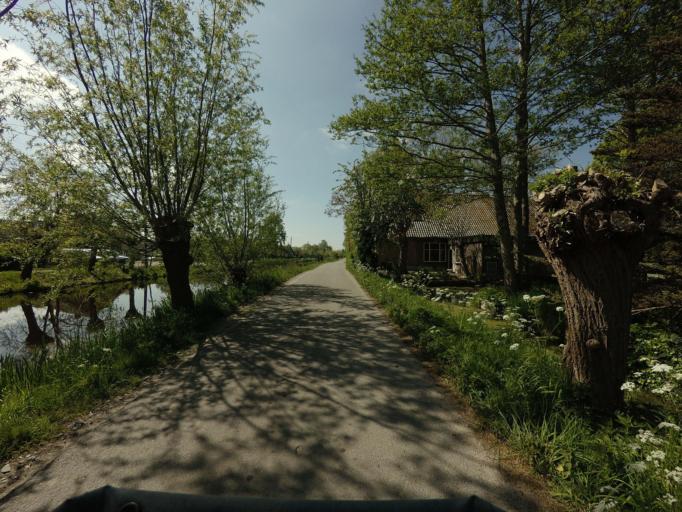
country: NL
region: South Holland
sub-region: Gemeente Gouda
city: Gouda
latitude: 51.9821
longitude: 4.7277
